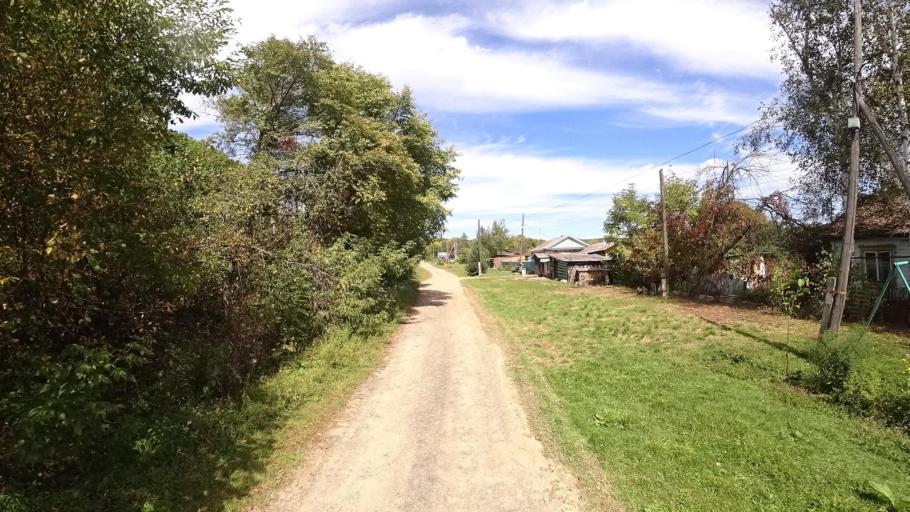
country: RU
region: Primorskiy
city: Yakovlevka
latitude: 44.6471
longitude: 133.5945
